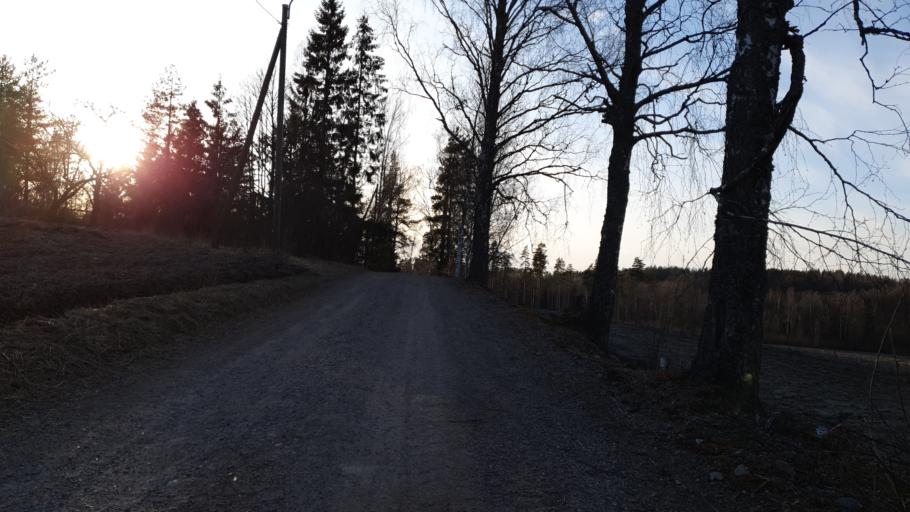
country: FI
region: Uusimaa
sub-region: Helsinki
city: Nurmijaervi
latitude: 60.3405
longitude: 24.8558
